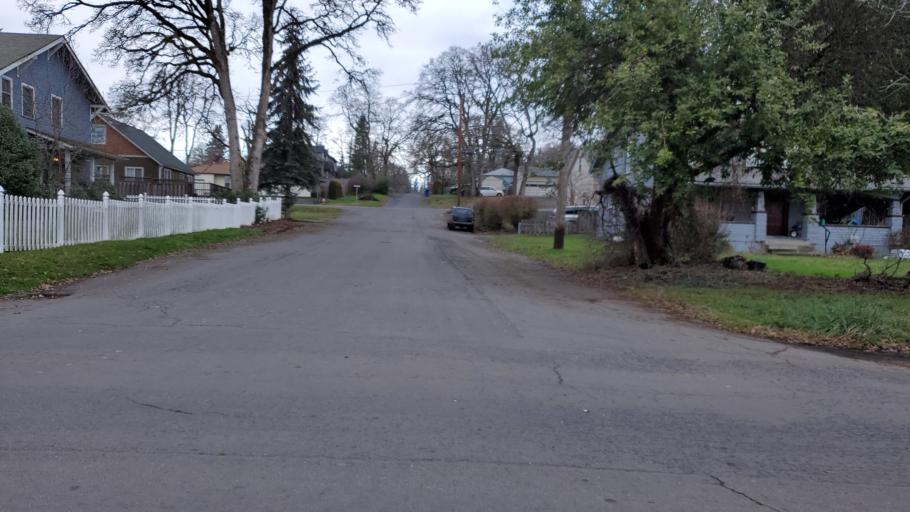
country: US
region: Oregon
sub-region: Clackamas County
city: Gladstone
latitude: 45.3836
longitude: -122.5869
